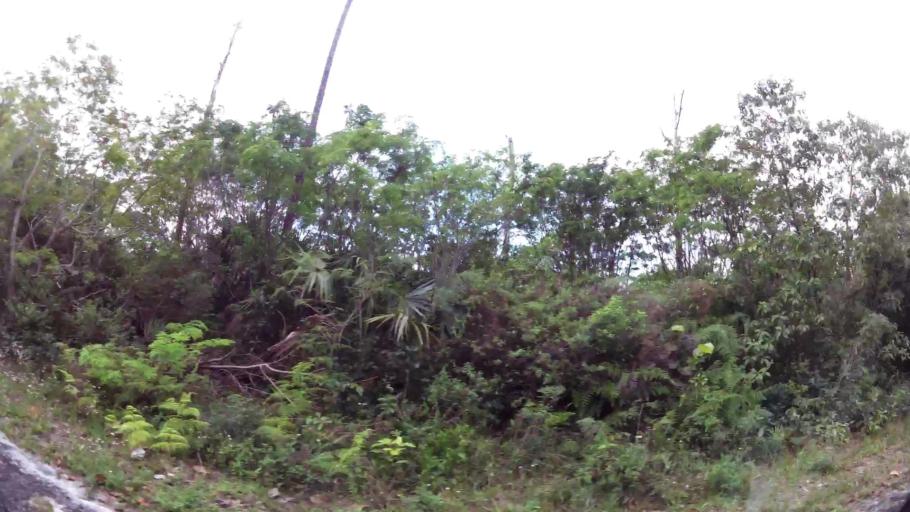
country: BS
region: Freeport
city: Lucaya
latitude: 26.5516
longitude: -78.5738
